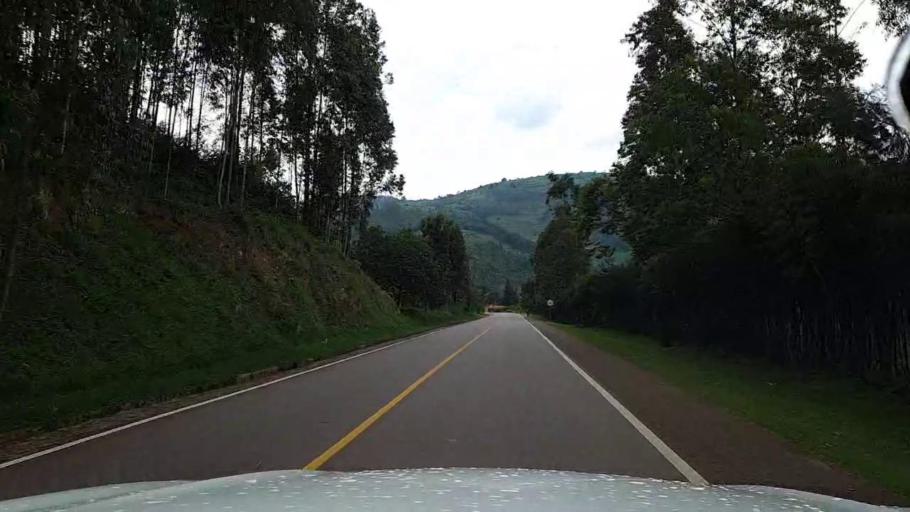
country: RW
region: Northern Province
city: Byumba
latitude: -1.7155
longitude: 30.1228
